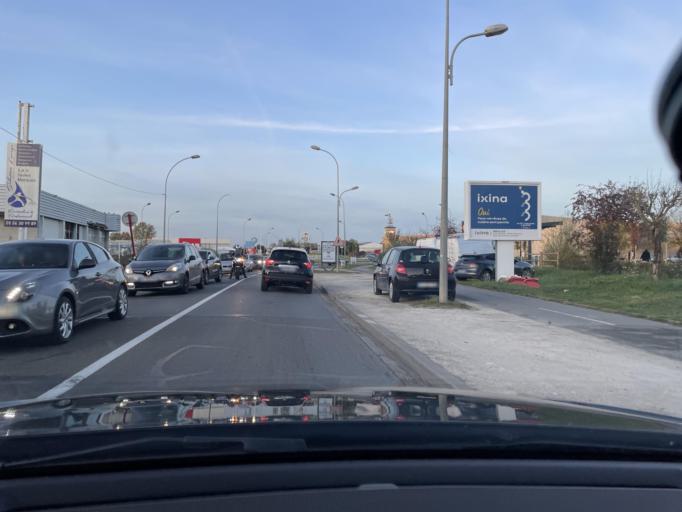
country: FR
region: Aquitaine
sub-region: Departement de la Gironde
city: Villenave-d'Ornon
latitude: 44.7881
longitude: -0.5360
